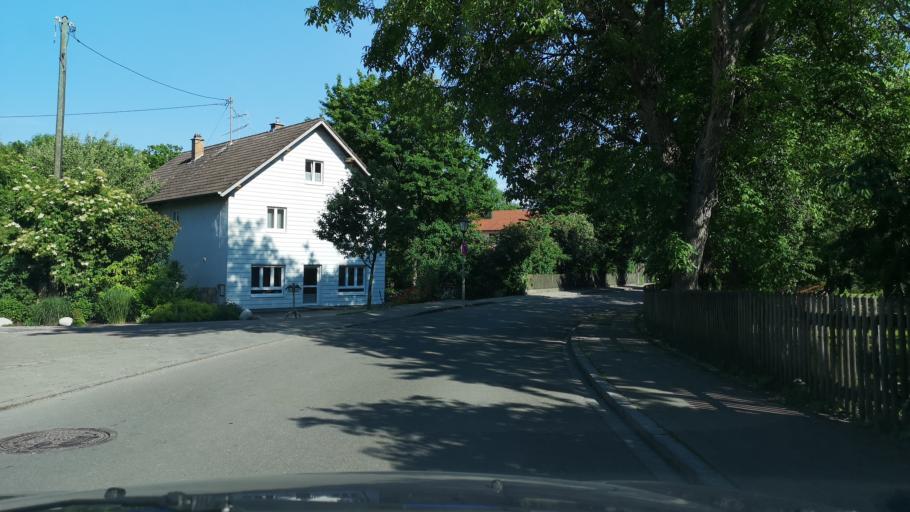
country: DE
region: Bavaria
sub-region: Upper Bavaria
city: Eichenried
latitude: 48.2463
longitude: 11.7795
